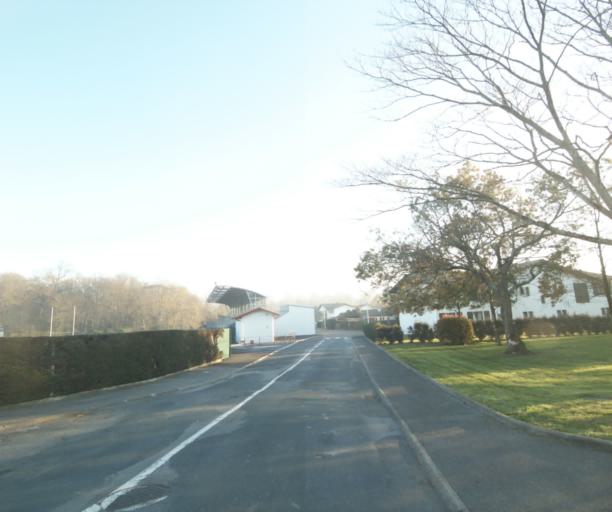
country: FR
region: Aquitaine
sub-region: Departement des Pyrenees-Atlantiques
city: Urrugne
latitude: 43.3656
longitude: -1.6943
